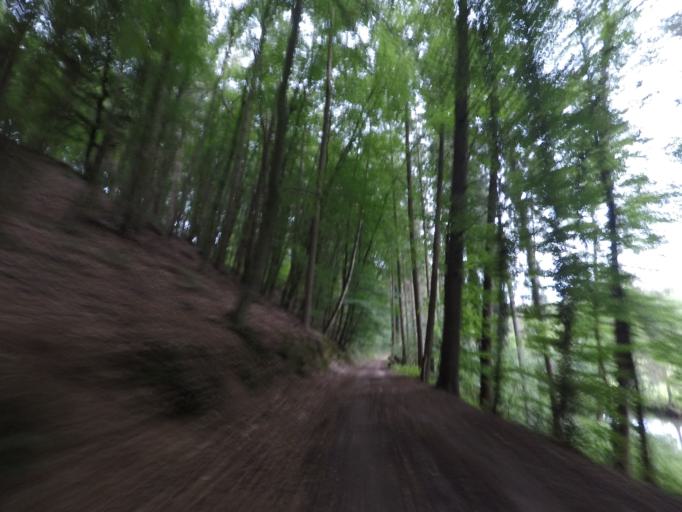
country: LU
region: Luxembourg
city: Itzig
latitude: 49.6052
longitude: 6.1672
